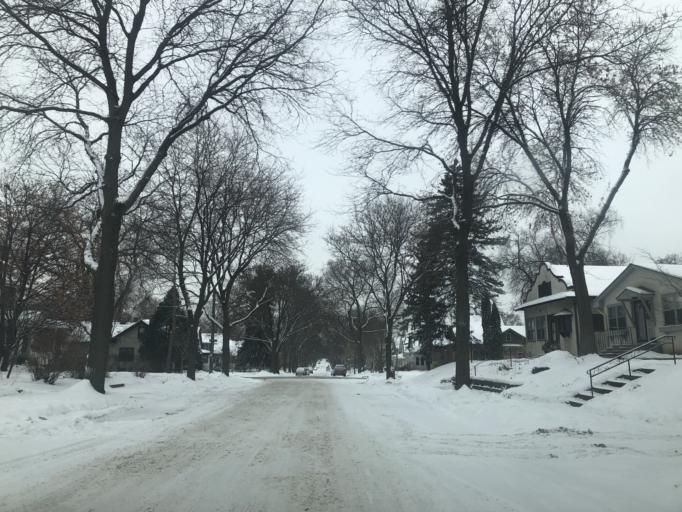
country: US
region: Minnesota
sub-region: Hennepin County
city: Richfield
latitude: 44.9274
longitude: -93.2806
